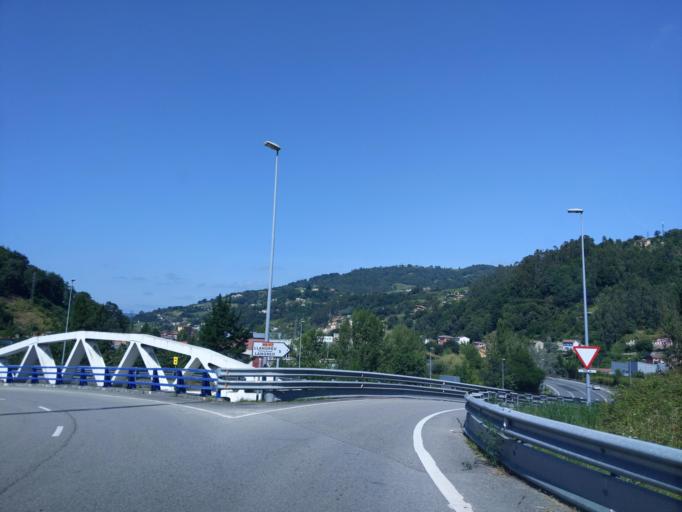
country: ES
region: Asturias
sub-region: Province of Asturias
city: El entrego
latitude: 43.2854
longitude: -5.6232
